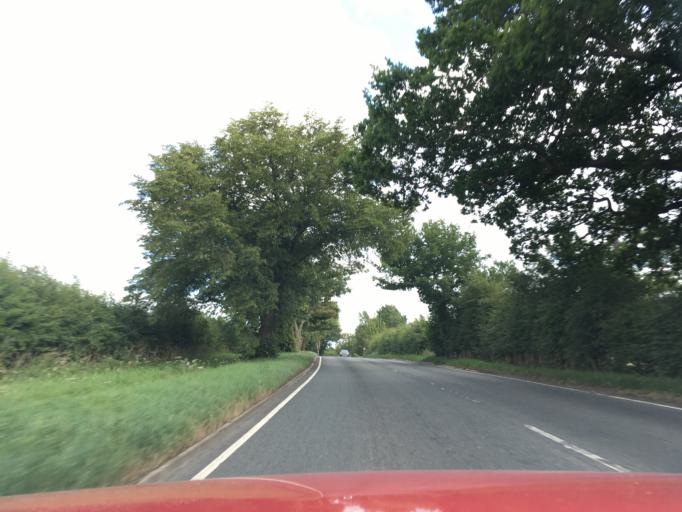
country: GB
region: England
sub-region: Warwickshire
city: Nuneaton
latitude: 52.5502
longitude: -1.4759
